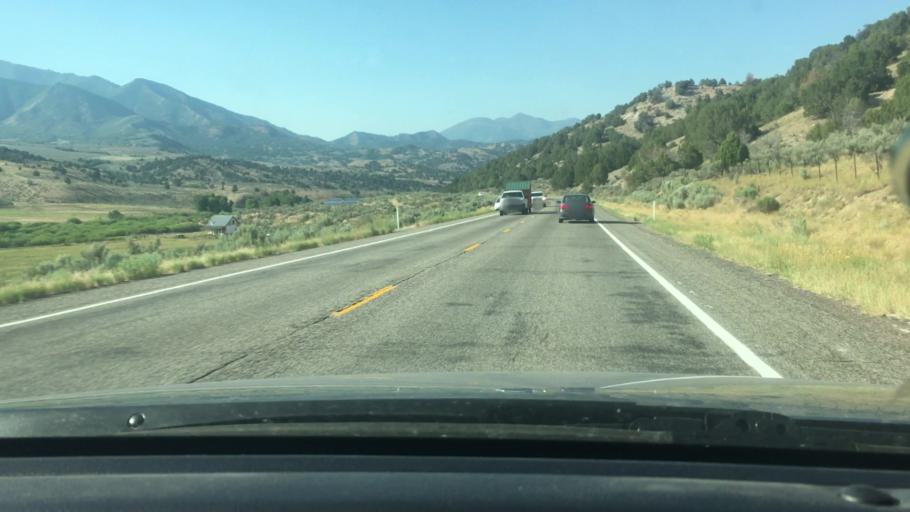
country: US
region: Utah
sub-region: Utah County
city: Woodland Hills
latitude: 39.9277
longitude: -111.5436
